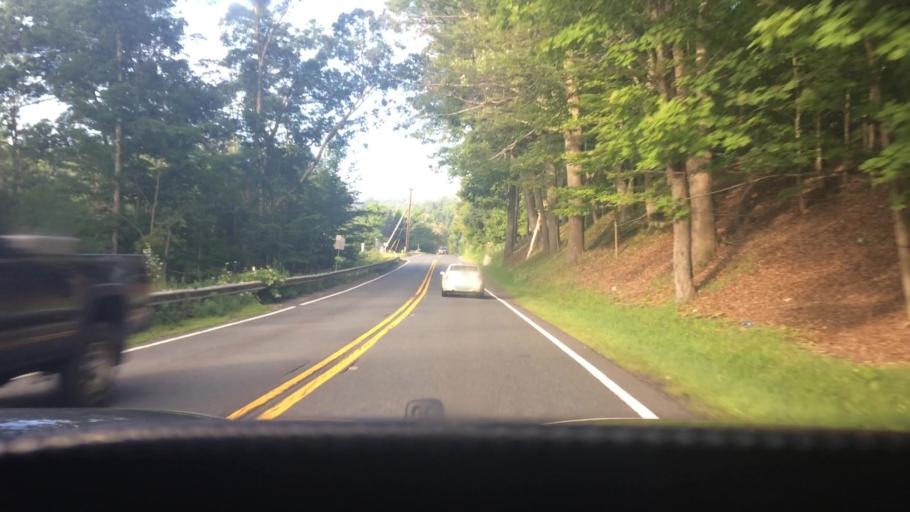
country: US
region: Massachusetts
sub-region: Franklin County
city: Erving
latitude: 42.6000
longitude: -72.4383
